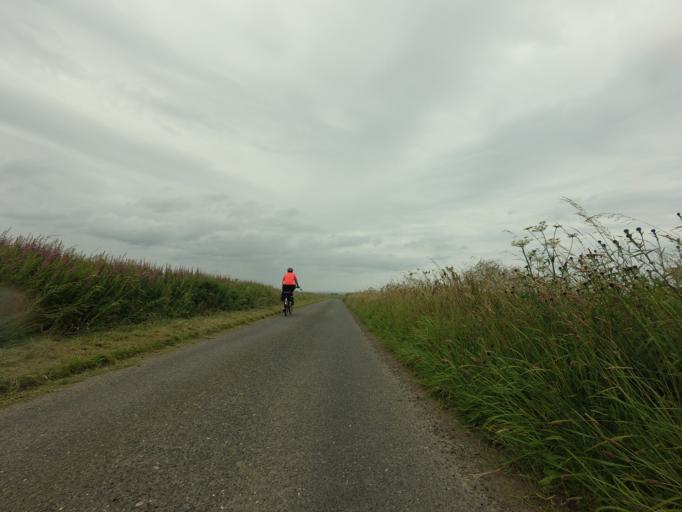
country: GB
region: Scotland
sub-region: Moray
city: Cullen
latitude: 57.6647
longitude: -2.7617
